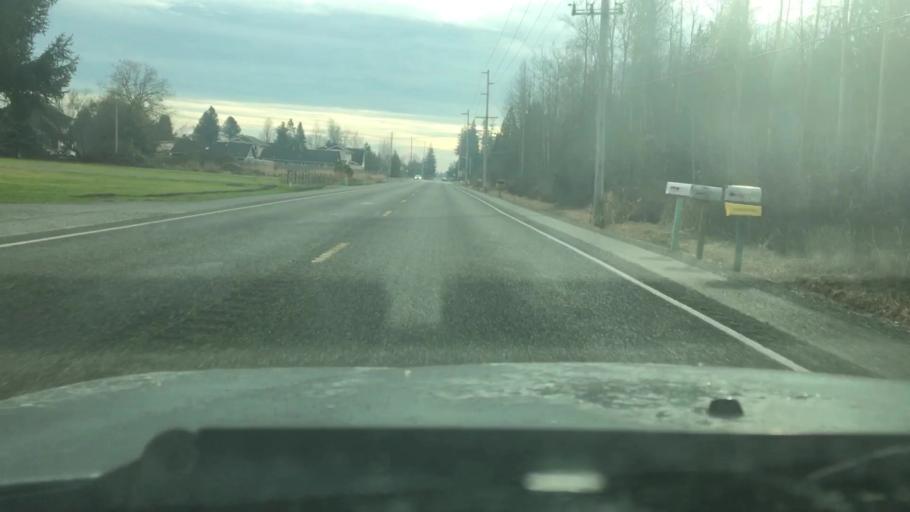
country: US
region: Washington
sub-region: Whatcom County
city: Ferndale
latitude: 48.8816
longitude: -122.5841
